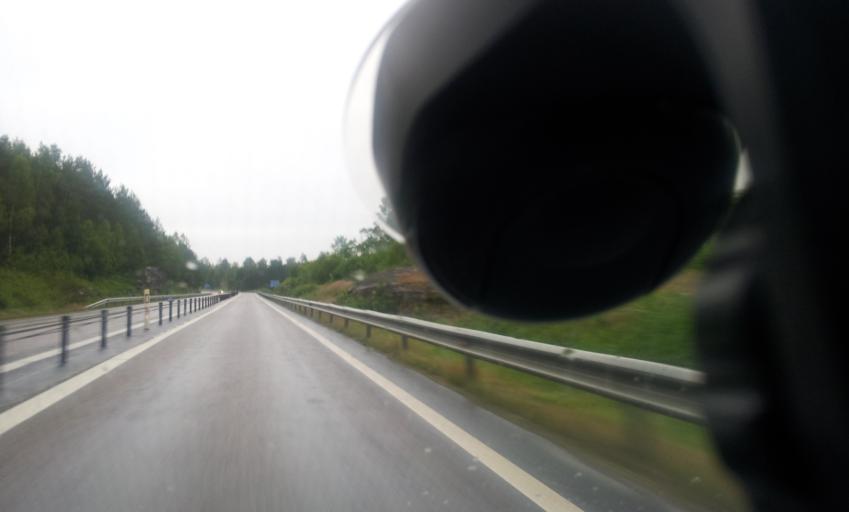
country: SE
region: Kalmar
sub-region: Vasterviks Kommun
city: Forserum
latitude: 58.0525
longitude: 16.5260
